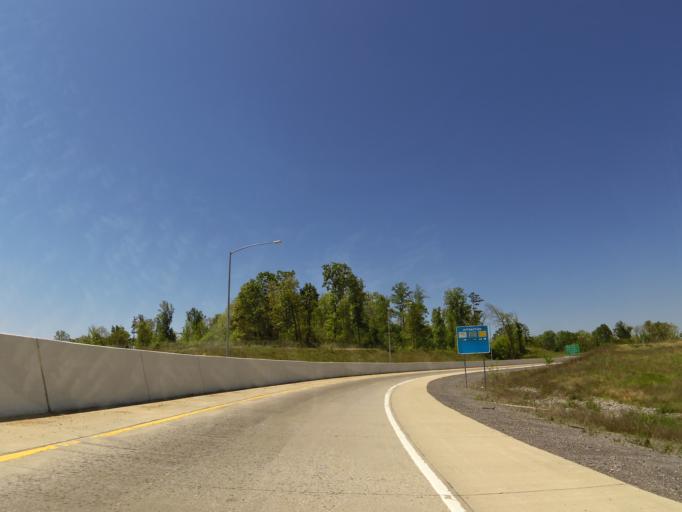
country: US
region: Tennessee
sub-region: Jefferson County
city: White Pine
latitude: 36.1339
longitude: -83.2776
